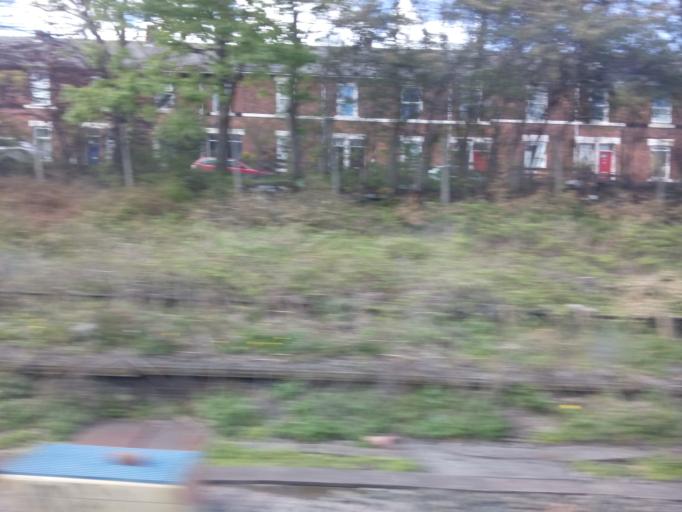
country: GB
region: England
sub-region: Gateshead
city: Gateshead
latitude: 54.9785
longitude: -1.5861
